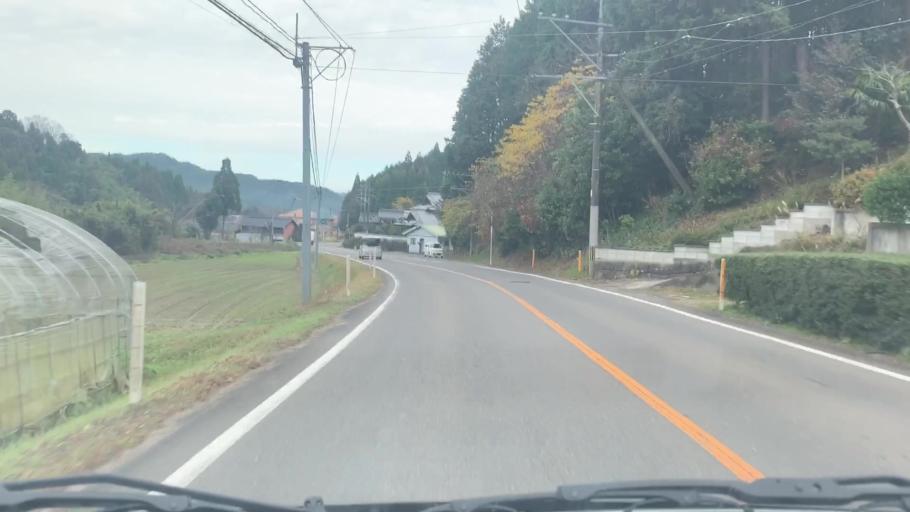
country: JP
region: Saga Prefecture
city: Takeocho-takeo
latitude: 33.1873
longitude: 129.9677
